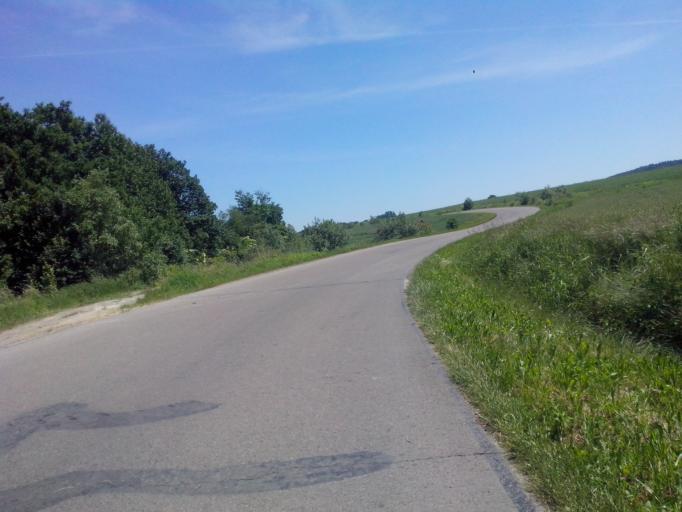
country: PL
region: Subcarpathian Voivodeship
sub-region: Powiat strzyzowski
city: Wisniowa
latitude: 49.8571
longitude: 21.6911
